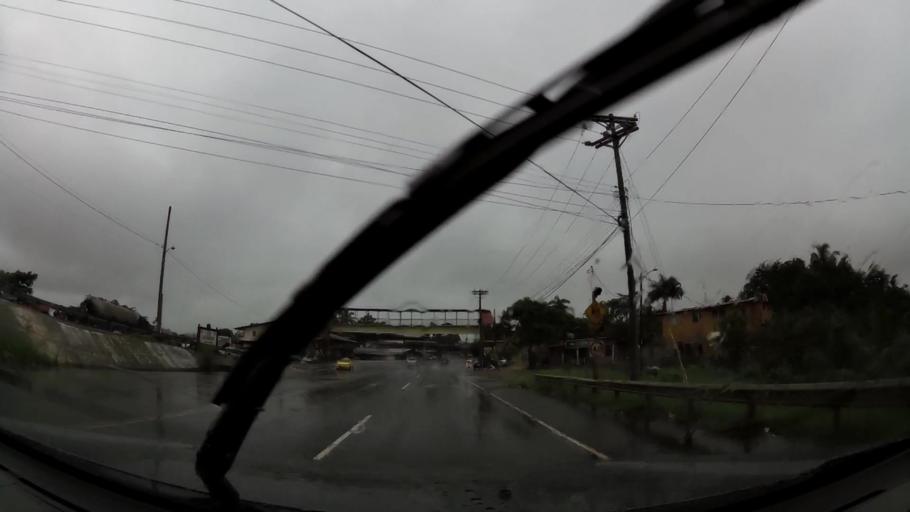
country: PA
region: Colon
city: Santa Rita Arriba
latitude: 9.3319
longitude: -79.8033
